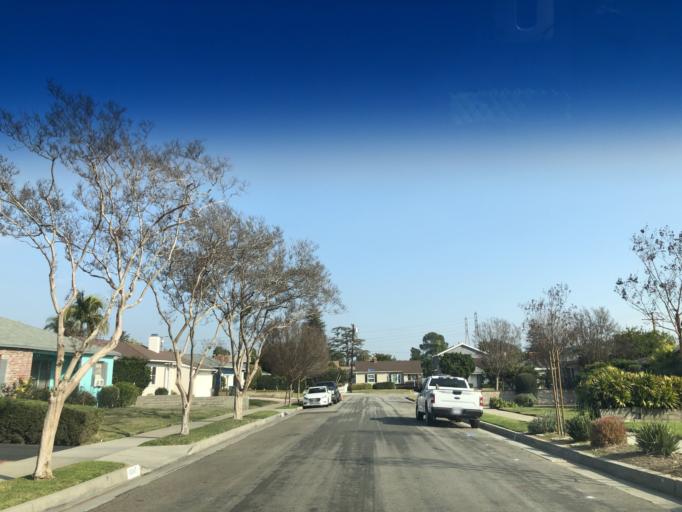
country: US
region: California
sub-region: Los Angeles County
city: East San Gabriel
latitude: 34.1090
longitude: -118.0874
